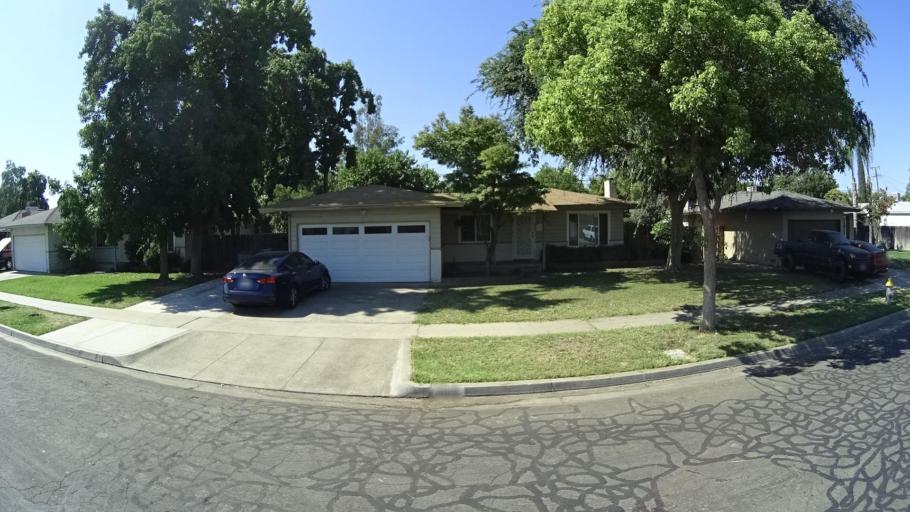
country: US
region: California
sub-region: Fresno County
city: Fresno
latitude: 36.7963
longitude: -119.7745
